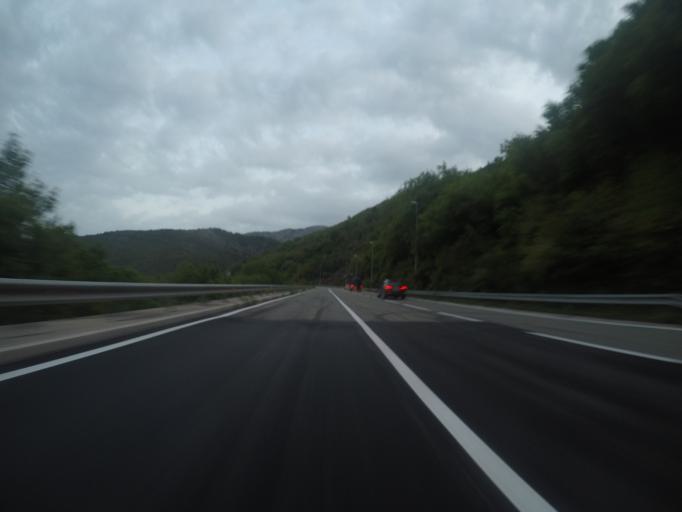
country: ME
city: Petrovac na Moru
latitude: 42.2069
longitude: 18.9495
